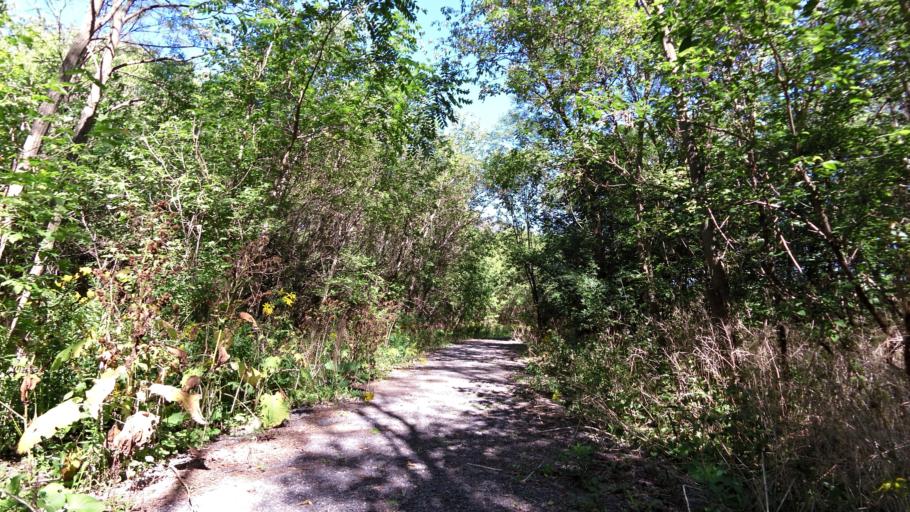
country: CA
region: Ontario
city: Etobicoke
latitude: 43.6469
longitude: -79.4977
